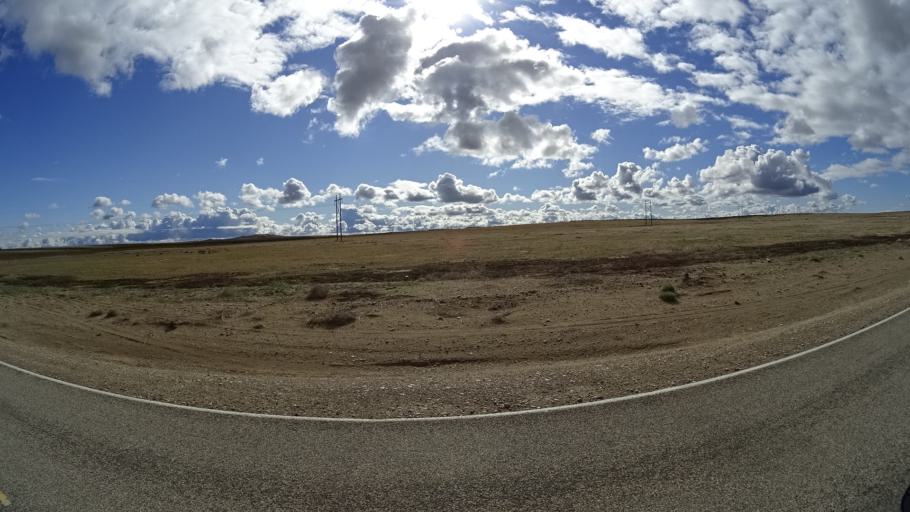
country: US
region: Idaho
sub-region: Owyhee County
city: Murphy
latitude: 43.2953
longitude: -116.3942
